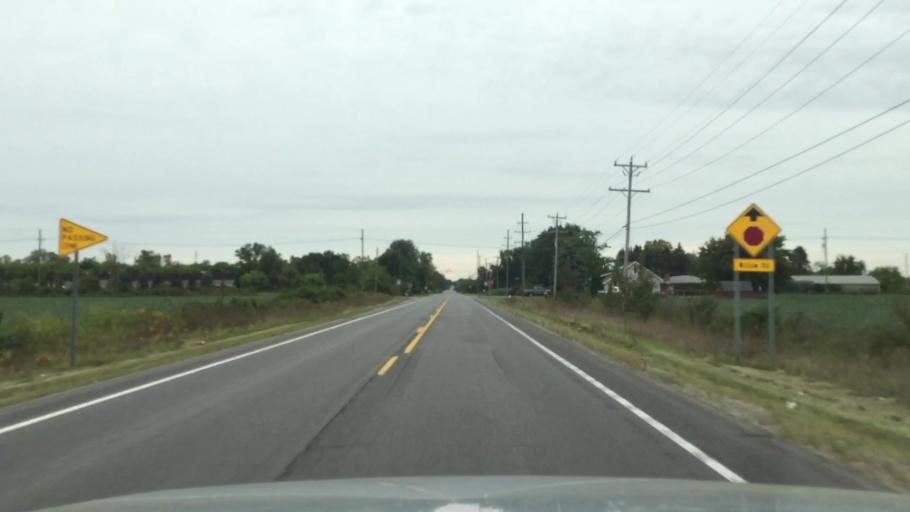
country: US
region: Michigan
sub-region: Washtenaw County
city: Milan
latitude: 42.1116
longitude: -83.6770
